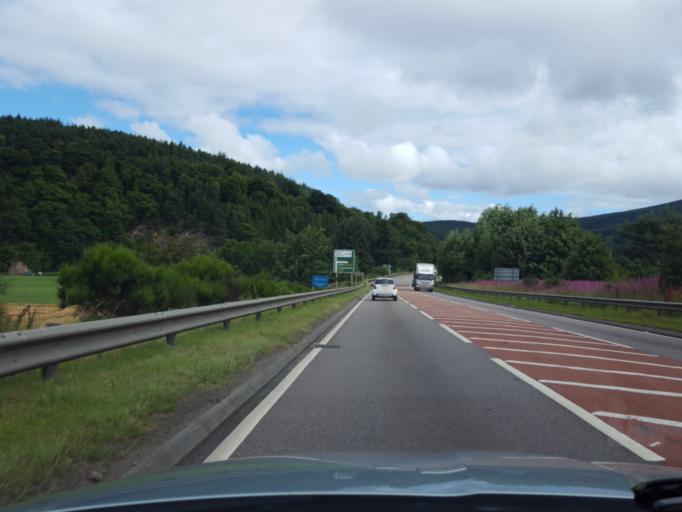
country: GB
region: Scotland
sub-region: Moray
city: Rothes
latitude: 57.4881
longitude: -3.1932
